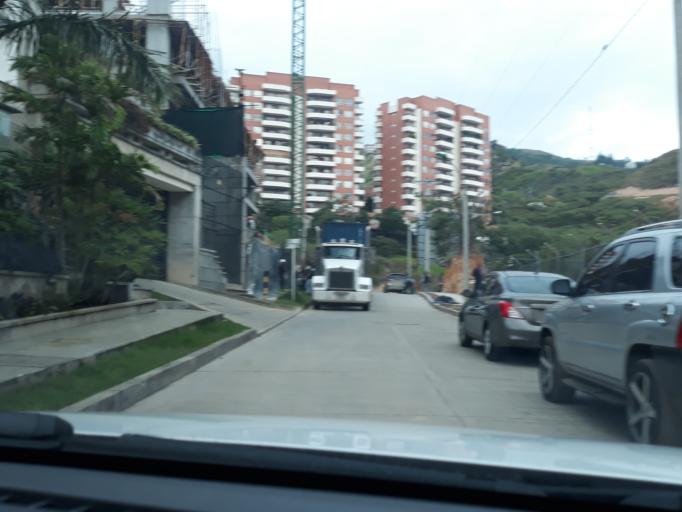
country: CO
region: Valle del Cauca
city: Cali
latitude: 3.4327
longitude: -76.5498
